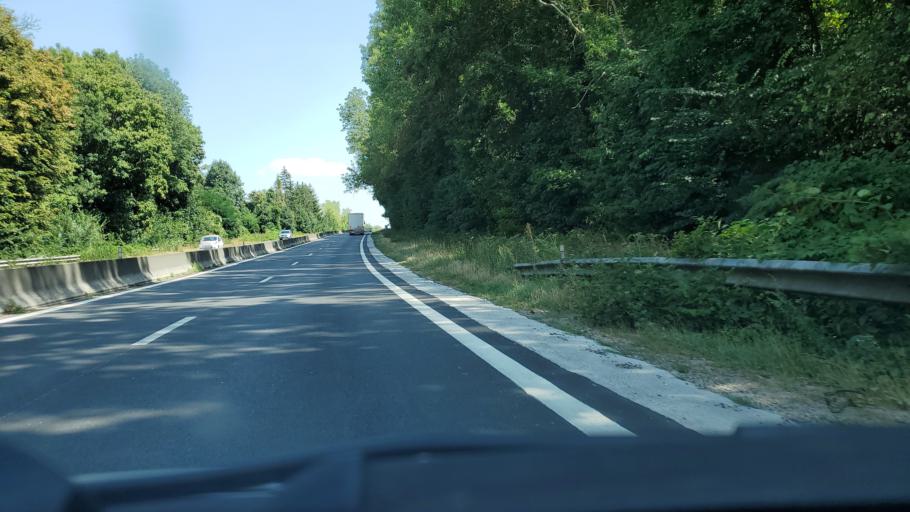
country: FR
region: Ile-de-France
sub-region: Departement de Seine-et-Marne
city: Tournan-en-Brie
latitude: 48.7368
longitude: 2.7631
